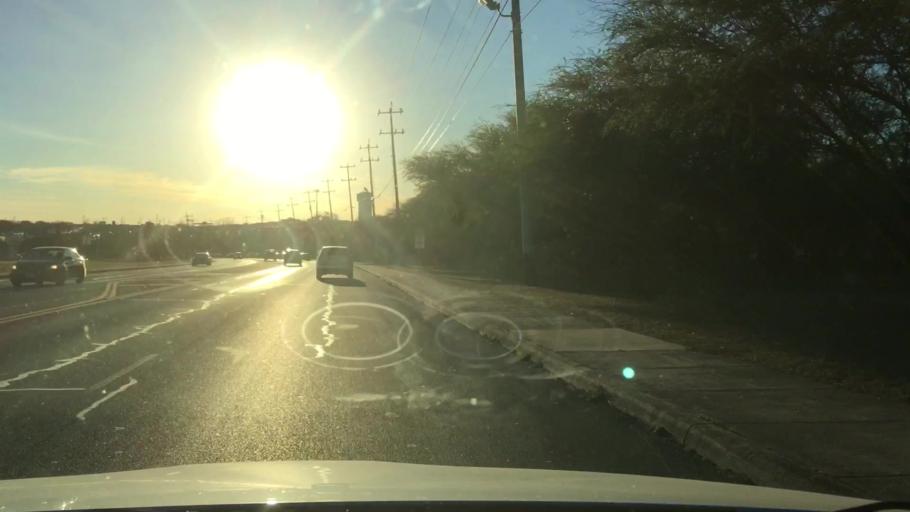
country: US
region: Texas
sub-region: Bexar County
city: Converse
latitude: 29.5415
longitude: -98.3245
